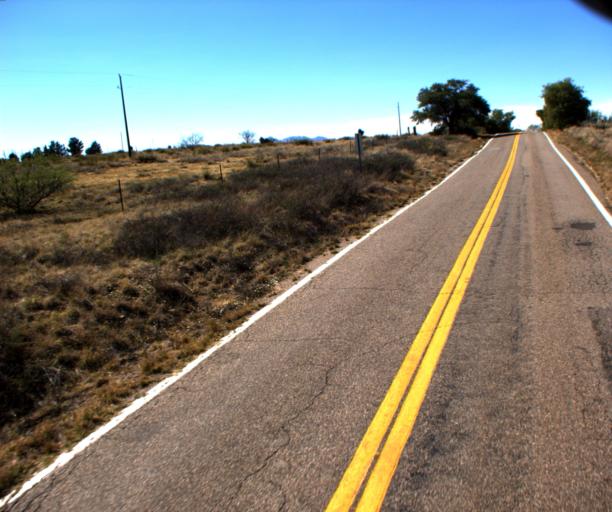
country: US
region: Arizona
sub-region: Cochise County
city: Huachuca City
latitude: 31.5831
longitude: -110.5601
